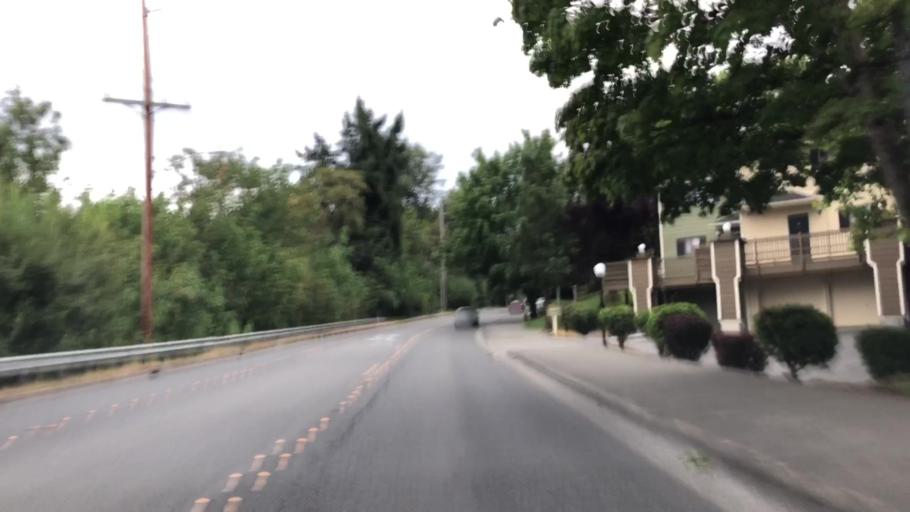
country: US
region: Washington
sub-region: King County
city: Redmond
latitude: 47.6785
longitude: -122.1387
